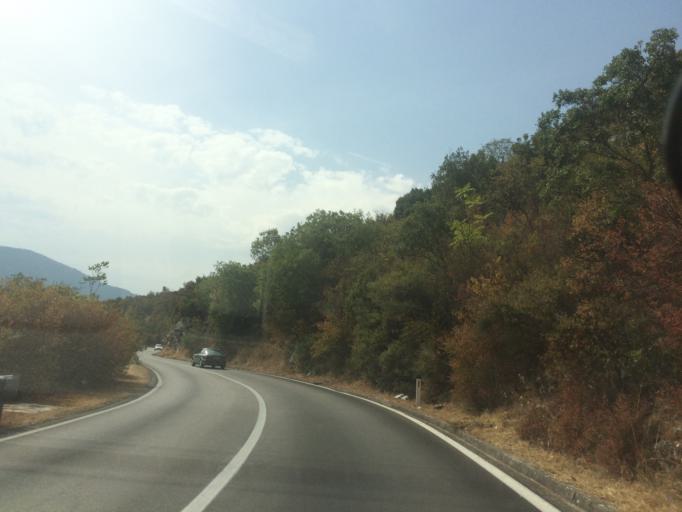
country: ME
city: Dobrota
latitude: 42.4857
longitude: 18.7420
